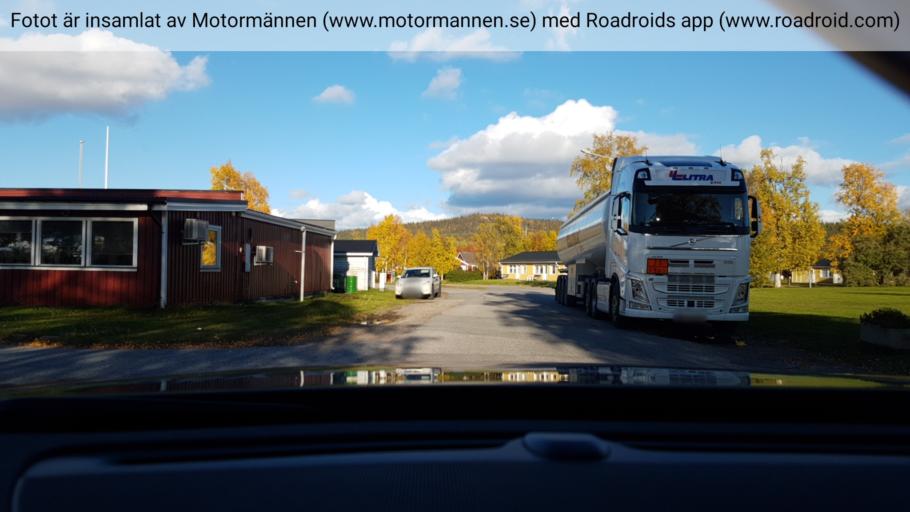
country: SE
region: Norrbotten
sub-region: Jokkmokks Kommun
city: Jokkmokk
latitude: 66.9602
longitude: 19.8224
